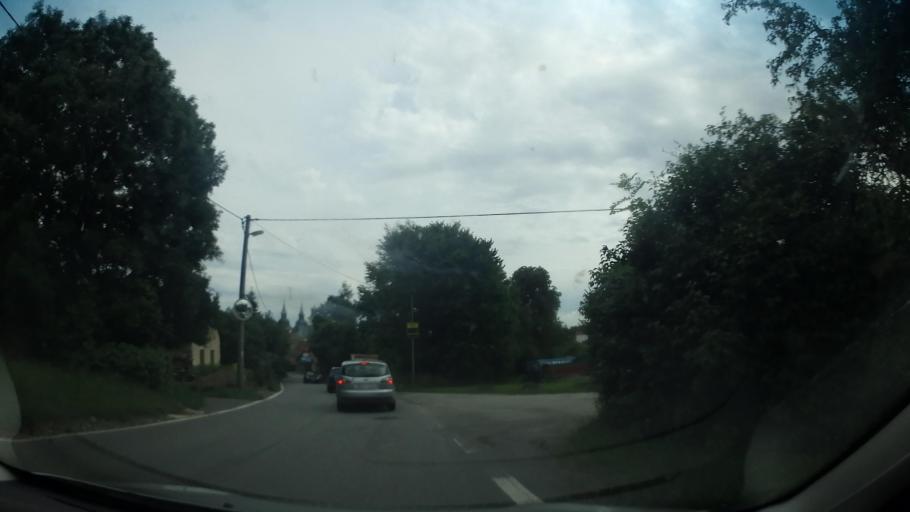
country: CZ
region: Vysocina
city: Bystrice nad Pernstejnem
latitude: 49.4958
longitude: 16.1756
